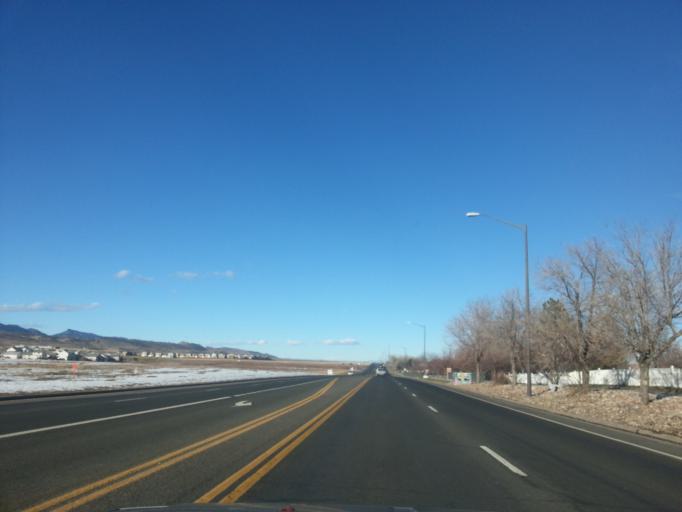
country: US
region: Colorado
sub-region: Larimer County
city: Loveland
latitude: 40.4284
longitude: -105.1156
